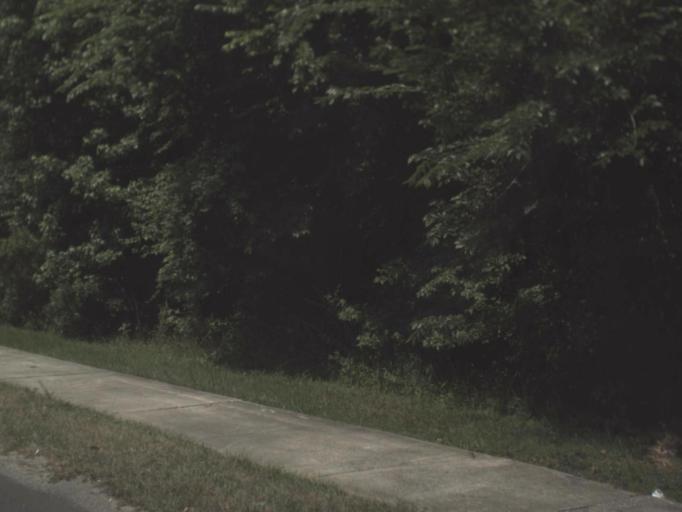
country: US
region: Florida
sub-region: Clay County
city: Green Cove Springs
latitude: 29.9866
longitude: -81.6770
